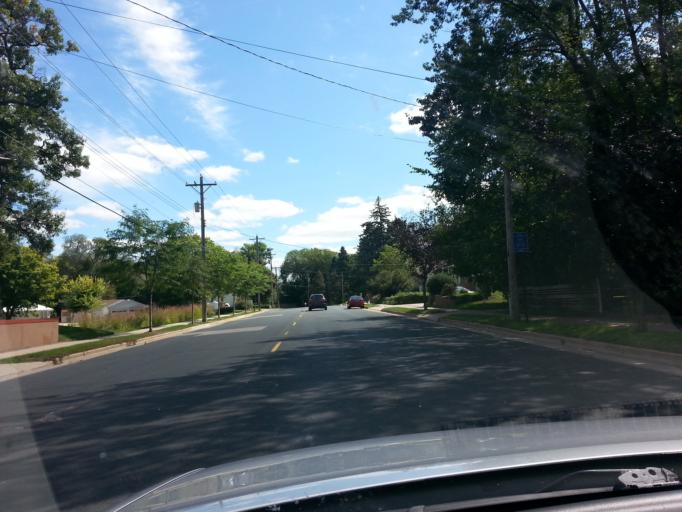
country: US
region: Minnesota
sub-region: Olmsted County
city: Rochester
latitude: 44.0369
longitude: -92.4606
